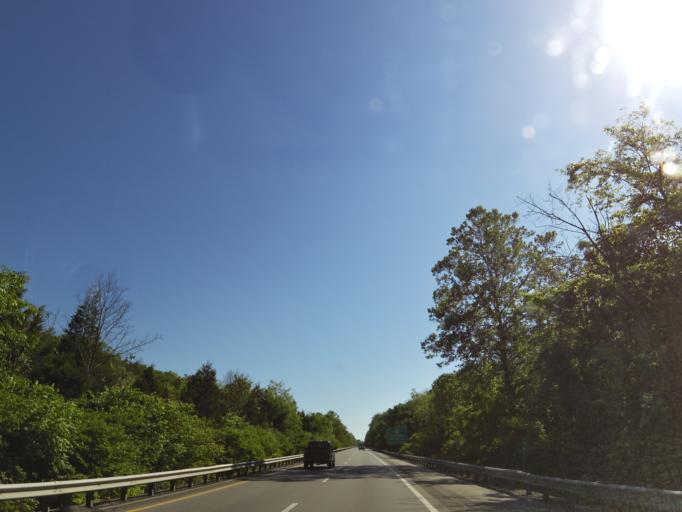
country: US
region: Kentucky
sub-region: Franklin County
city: Frankfort
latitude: 38.1639
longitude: -84.8440
